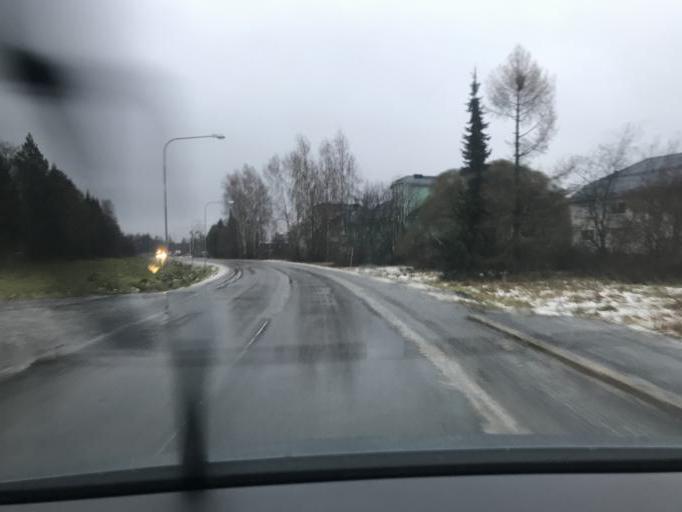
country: SE
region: Norrbotten
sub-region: Lulea Kommun
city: Bergnaset
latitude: 65.6181
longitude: 22.1228
